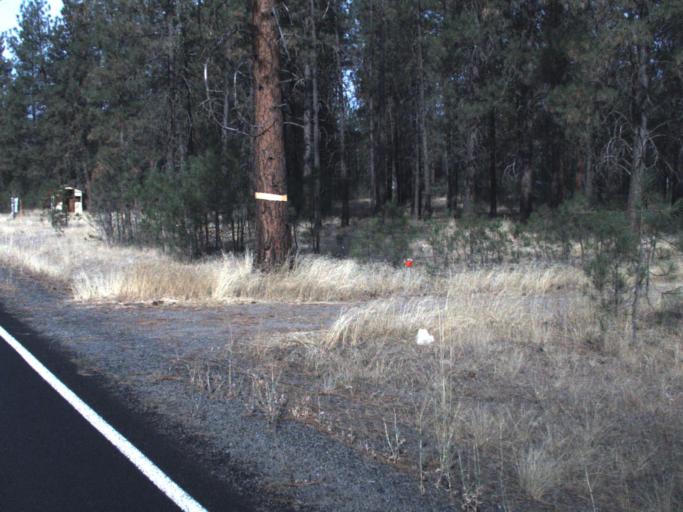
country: US
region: Washington
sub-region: Spokane County
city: Fairchild Air Force Base
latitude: 47.8392
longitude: -117.8214
